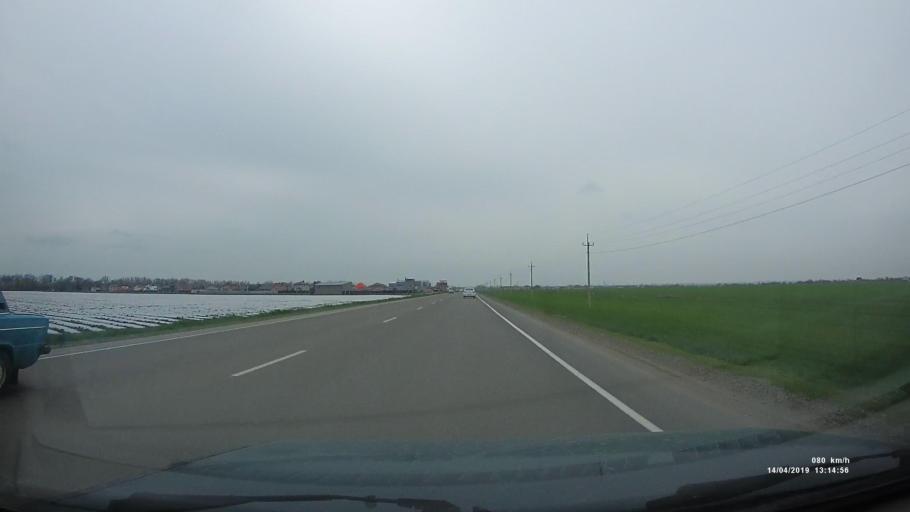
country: RU
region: Rostov
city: Kuleshovka
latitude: 47.0874
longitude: 39.6020
